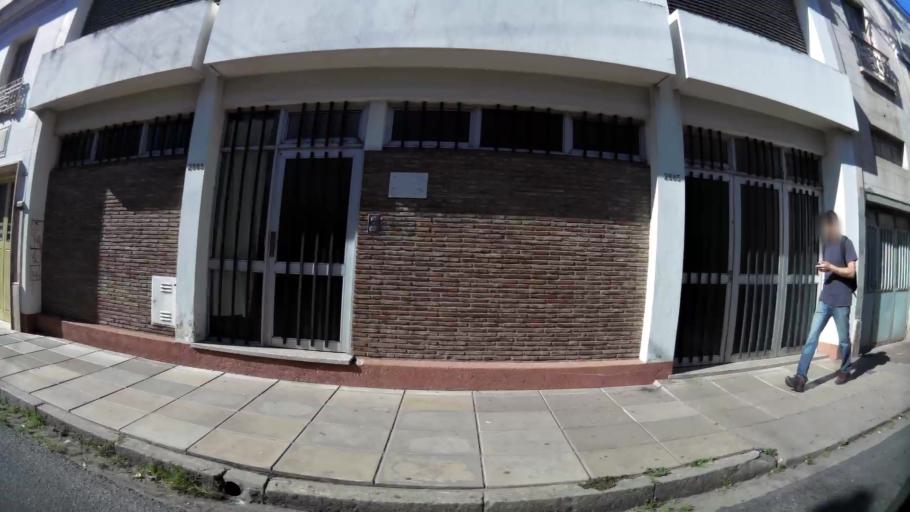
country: AR
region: Santa Fe
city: Santa Fe de la Vera Cruz
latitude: -31.6445
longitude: -60.7113
